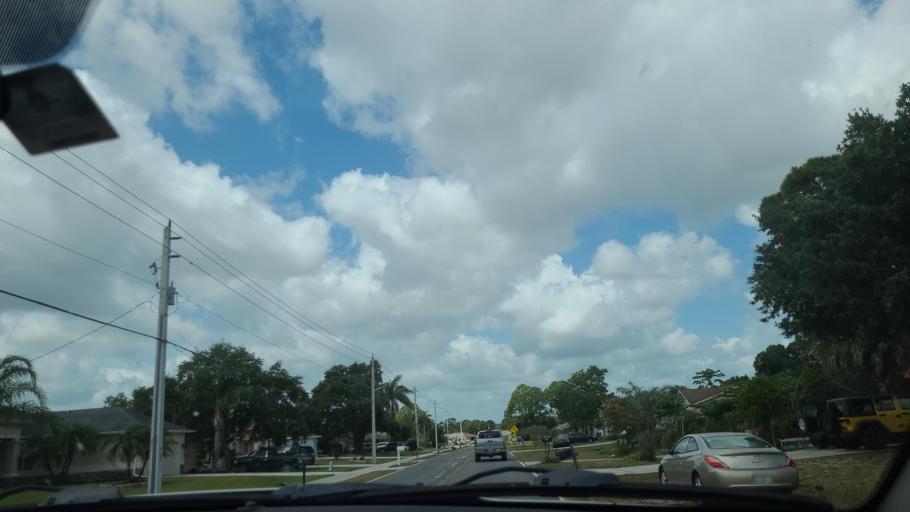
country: US
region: Florida
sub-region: Brevard County
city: June Park
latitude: 28.0110
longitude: -80.6817
